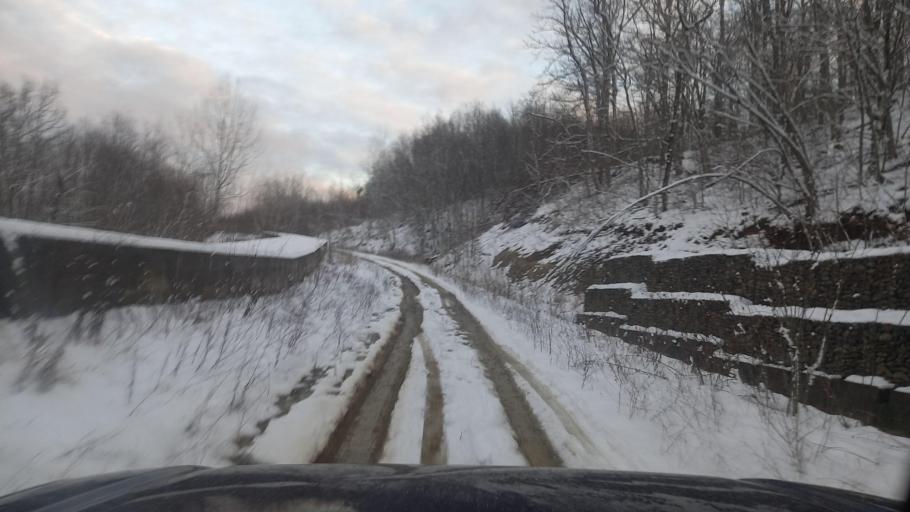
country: RU
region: Krasnodarskiy
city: Smolenskaya
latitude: 44.6723
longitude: 38.7886
